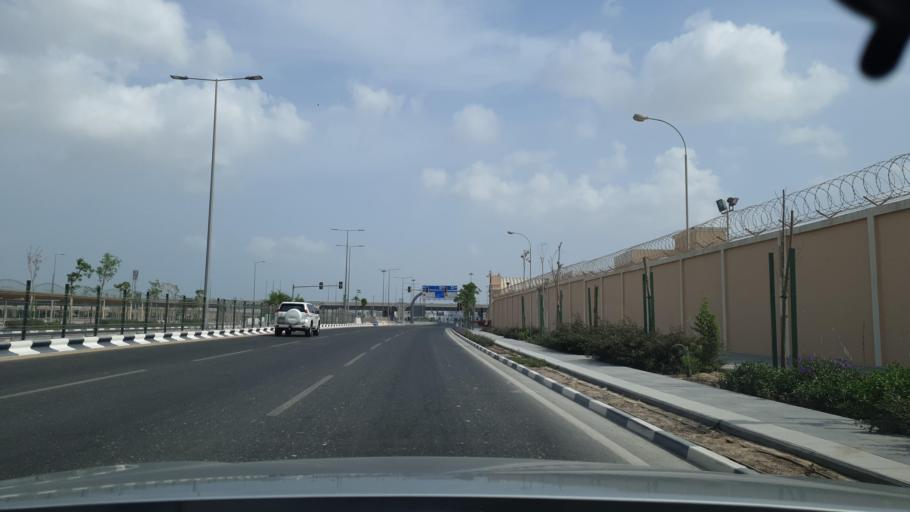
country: QA
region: Baladiyat ar Rayyan
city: Ar Rayyan
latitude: 25.2783
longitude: 51.4678
